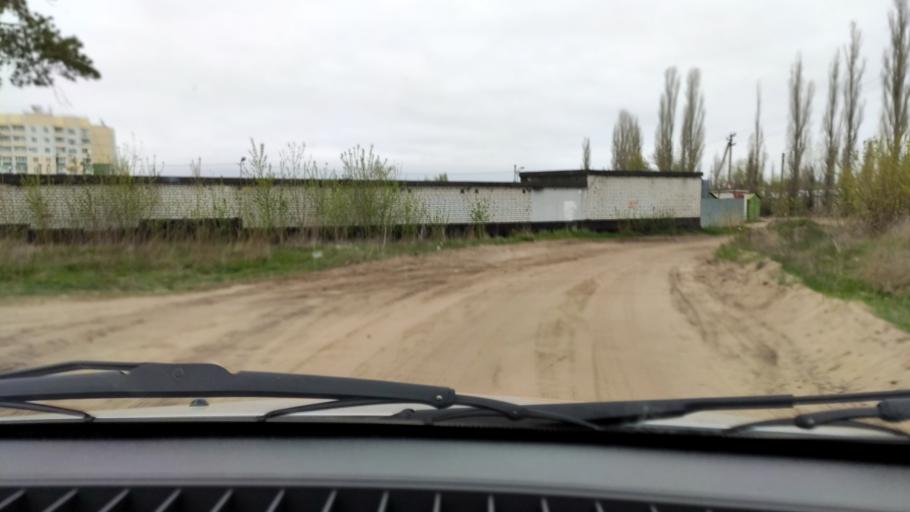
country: RU
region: Voronezj
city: Pridonskoy
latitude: 51.6199
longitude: 39.0687
